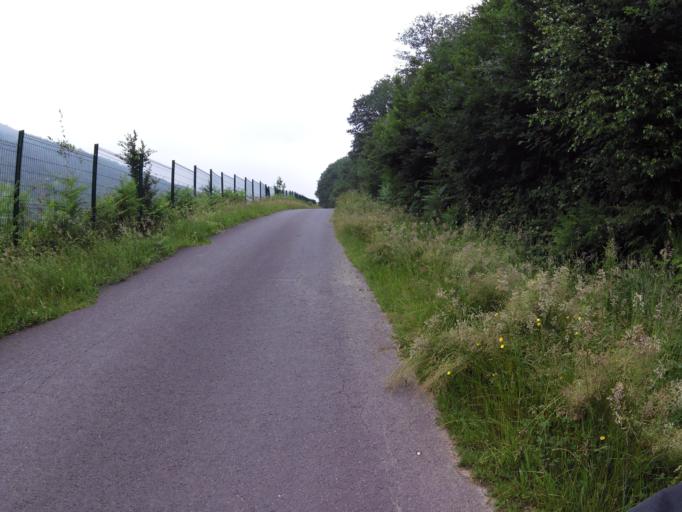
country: FR
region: Champagne-Ardenne
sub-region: Departement des Ardennes
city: Revin
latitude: 49.9538
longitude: 4.6556
